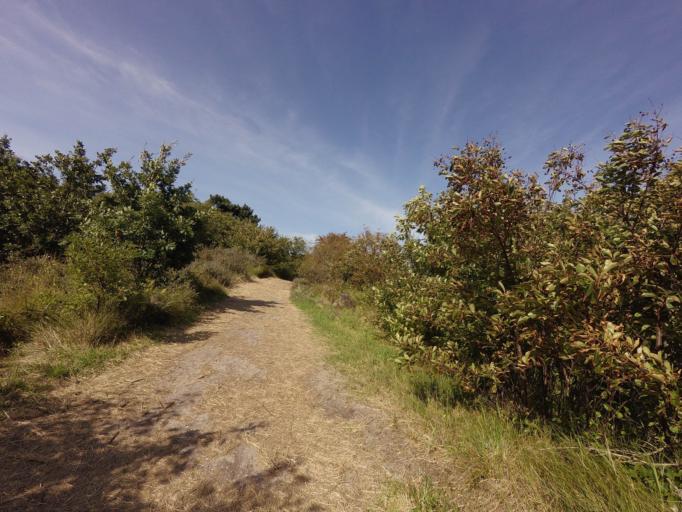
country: NL
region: Friesland
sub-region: Gemeente Ameland
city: Nes
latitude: 53.4546
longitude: 5.7686
